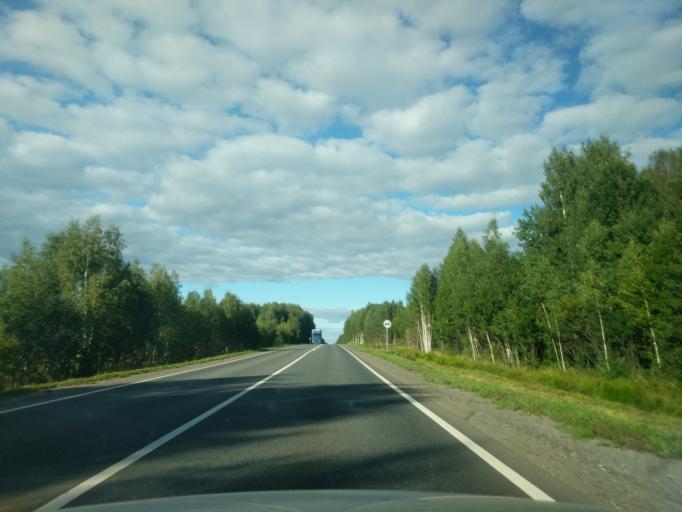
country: RU
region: Kostroma
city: Manturovo
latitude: 58.2079
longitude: 44.6017
